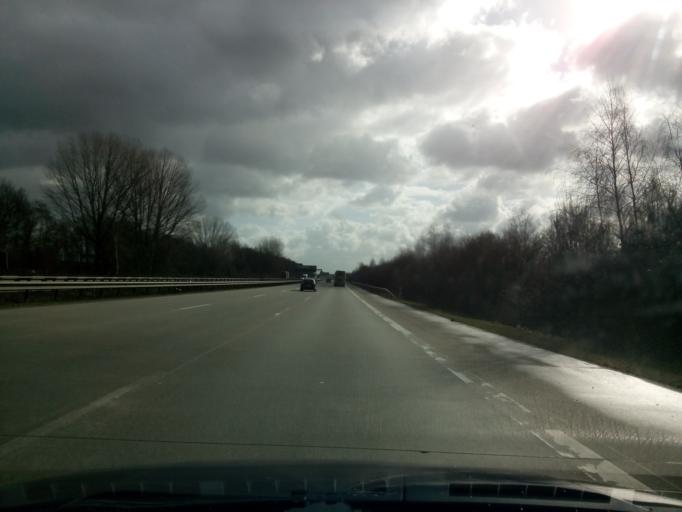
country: DE
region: Lower Saxony
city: Ritterhude
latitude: 53.1370
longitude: 8.7472
